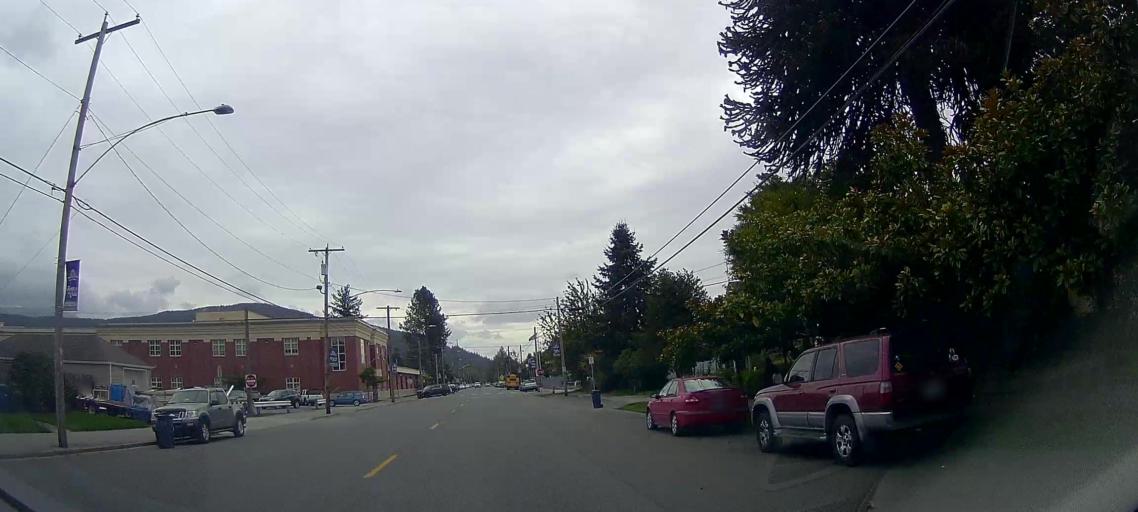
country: US
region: Washington
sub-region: Skagit County
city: Sedro-Woolley
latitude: 48.5014
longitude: -122.2375
